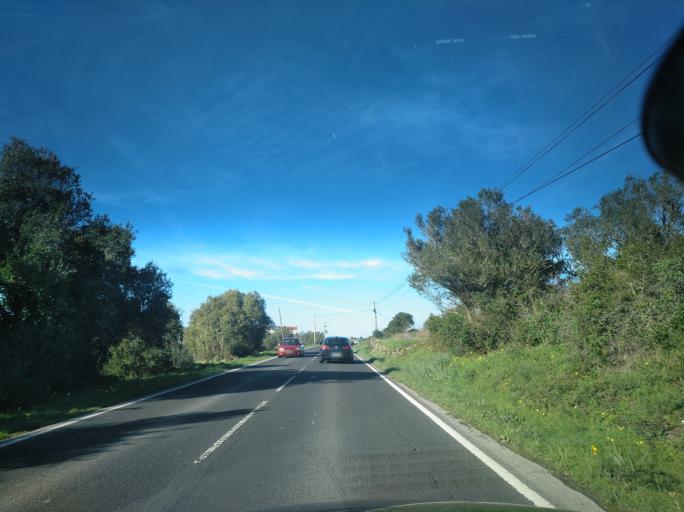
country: PT
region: Lisbon
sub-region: Mafra
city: Mafra
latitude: 38.9049
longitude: -9.3289
